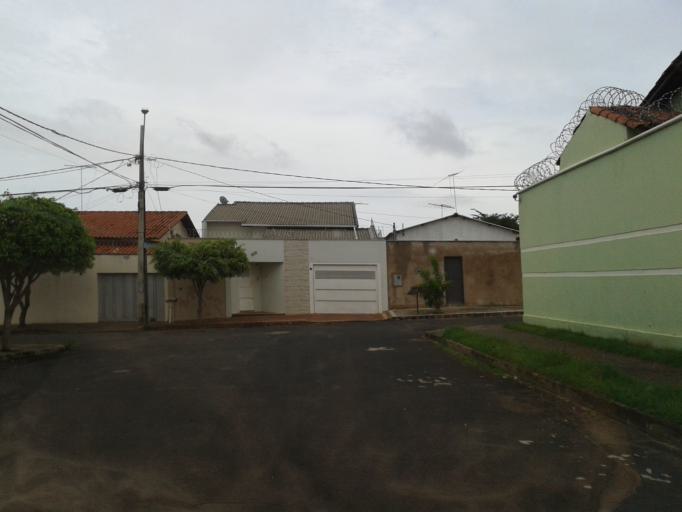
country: BR
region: Minas Gerais
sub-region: Uberlandia
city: Uberlandia
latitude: -18.9336
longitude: -48.2468
